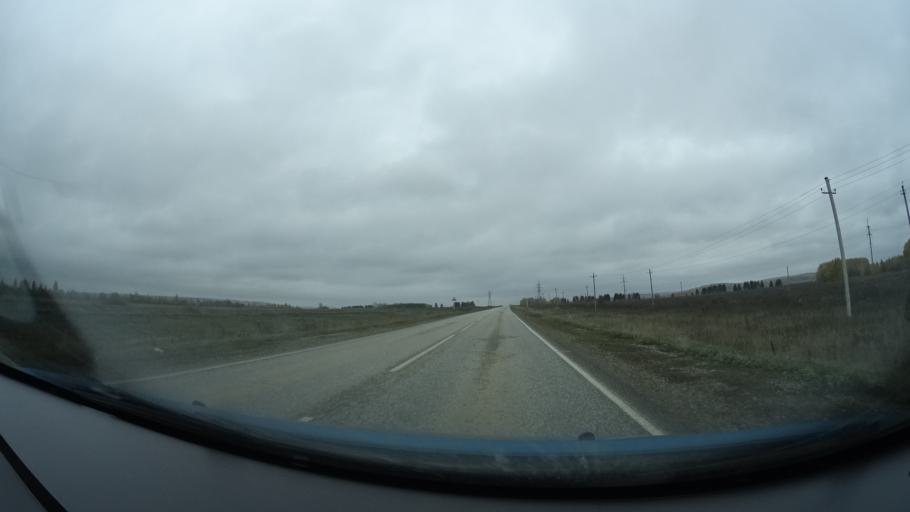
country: RU
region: Perm
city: Barda
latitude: 57.0788
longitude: 55.5428
